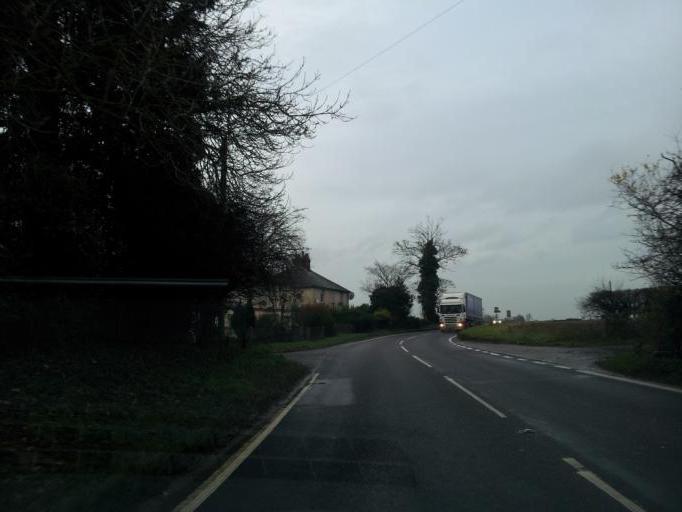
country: GB
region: England
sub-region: Norfolk
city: Martham
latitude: 52.6739
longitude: 1.5929
